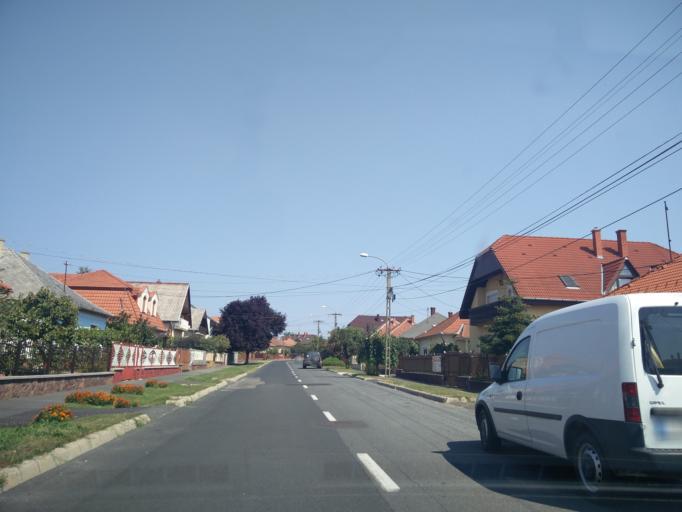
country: HU
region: Zala
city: Zalaegerszeg
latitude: 46.8304
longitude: 16.8307
